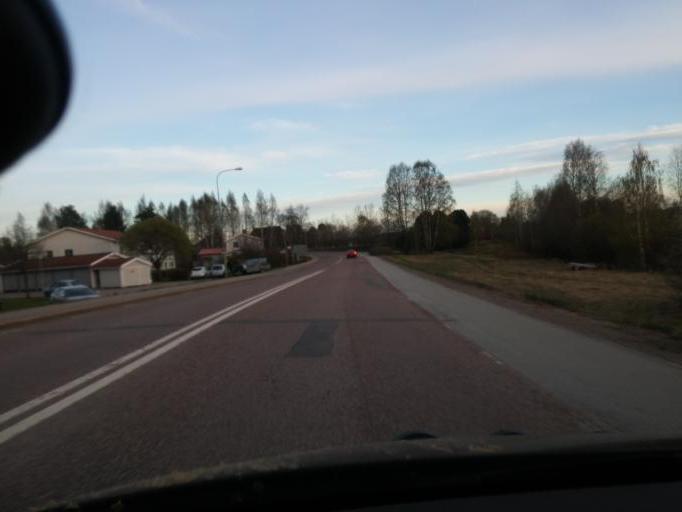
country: SE
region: Gaevleborg
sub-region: Ljusdals Kommun
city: Ljusdal
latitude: 61.8330
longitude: 16.0687
